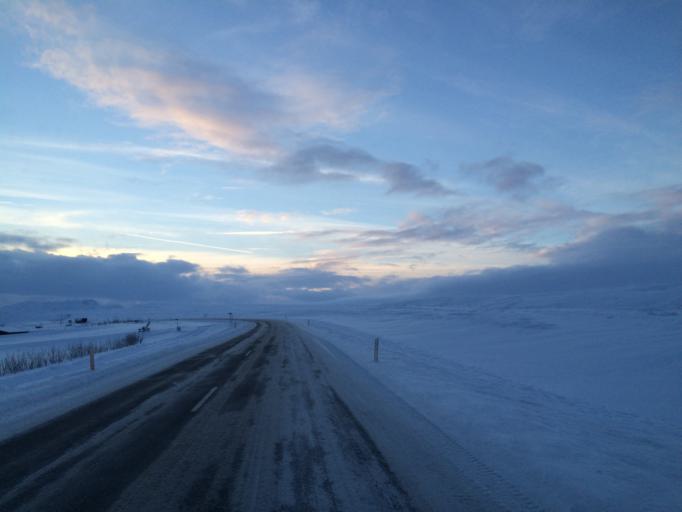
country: IS
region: South
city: Hveragerdi
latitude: 64.2345
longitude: -21.1950
